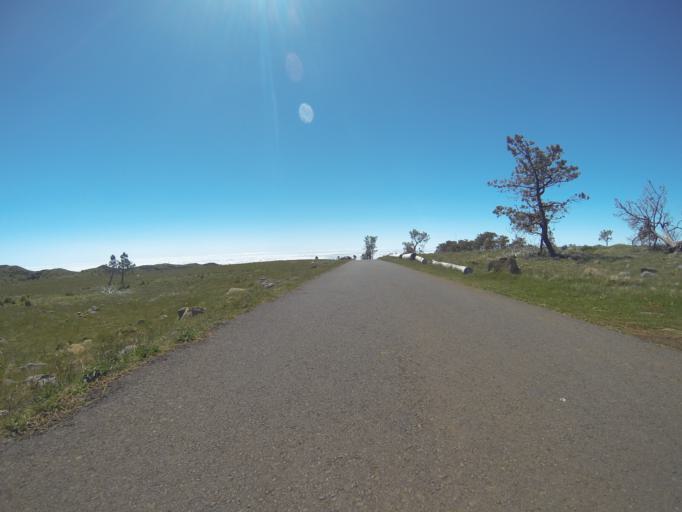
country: PT
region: Madeira
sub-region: Funchal
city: Nossa Senhora do Monte
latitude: 32.7159
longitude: -16.9112
